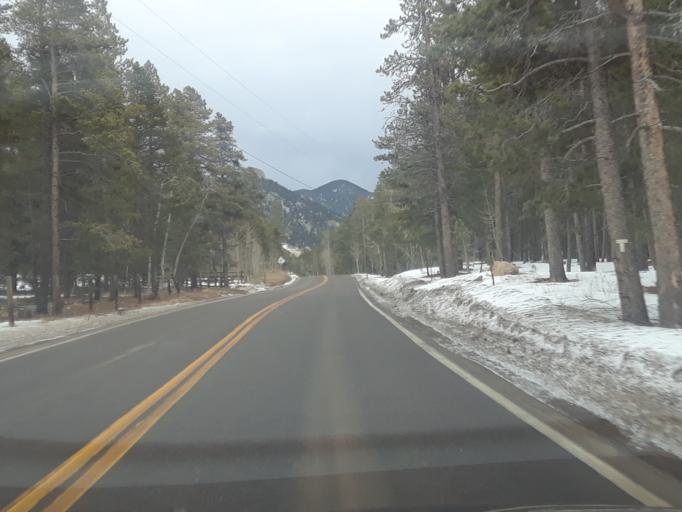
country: US
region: Colorado
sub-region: Gilpin County
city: Central City
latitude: 39.8406
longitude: -105.4523
